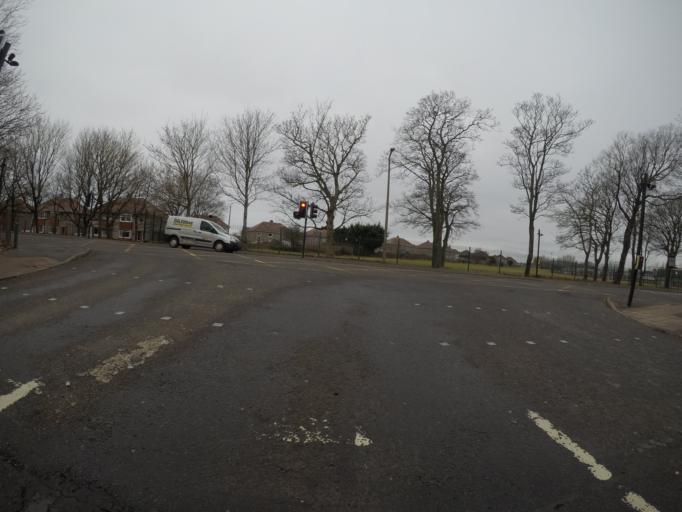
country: GB
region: Scotland
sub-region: North Ayrshire
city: Irvine
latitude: 55.6265
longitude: -4.6733
